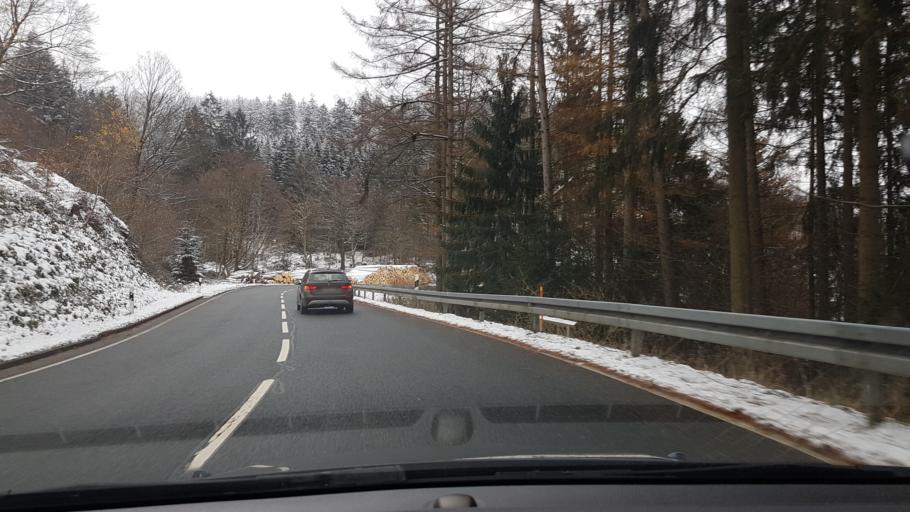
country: DE
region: Lower Saxony
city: Bad Grund
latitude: 51.8111
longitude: 10.2462
